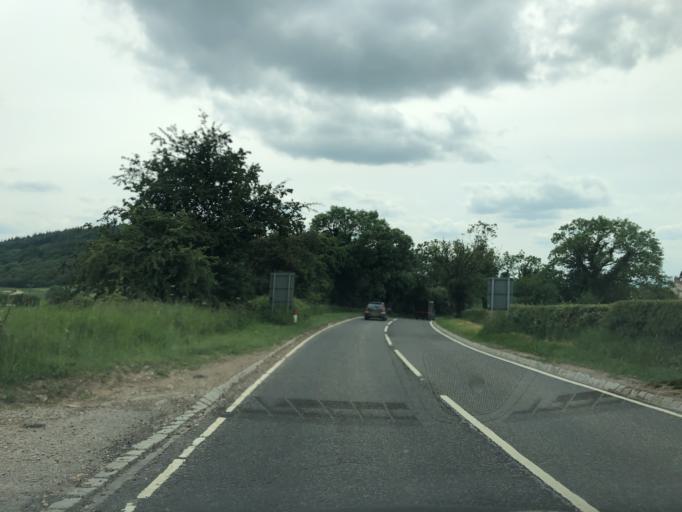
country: GB
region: England
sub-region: North Yorkshire
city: Angram Grange
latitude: 54.2371
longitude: -1.2200
